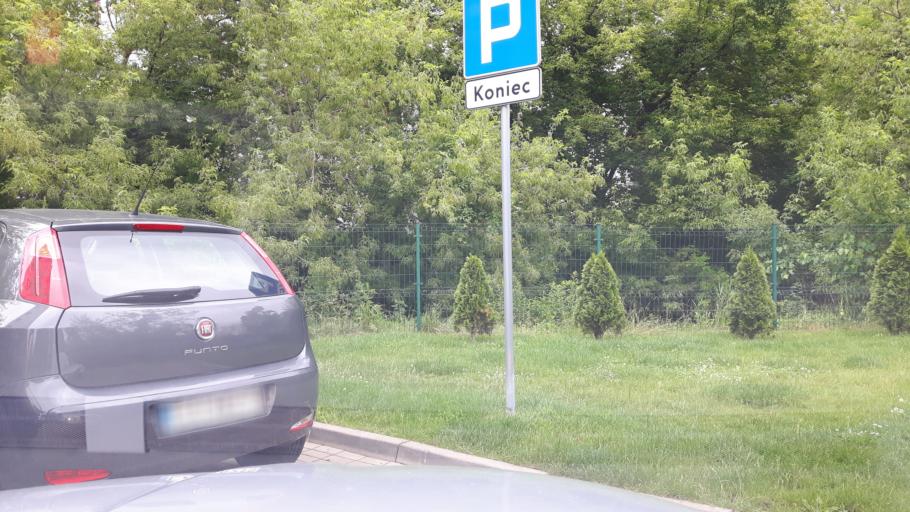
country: PL
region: Masovian Voivodeship
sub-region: Warszawa
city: Zoliborz
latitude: 52.2580
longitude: 20.9767
